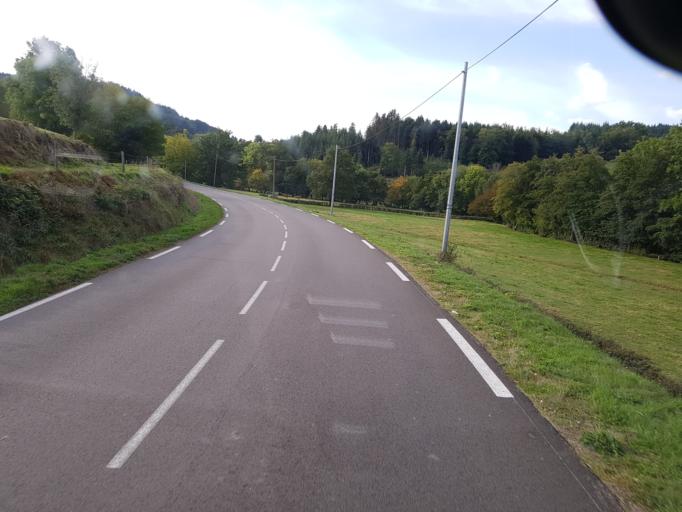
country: FR
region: Bourgogne
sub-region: Departement de Saone-et-Loire
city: La Clayette
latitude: 46.2756
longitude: 4.3735
